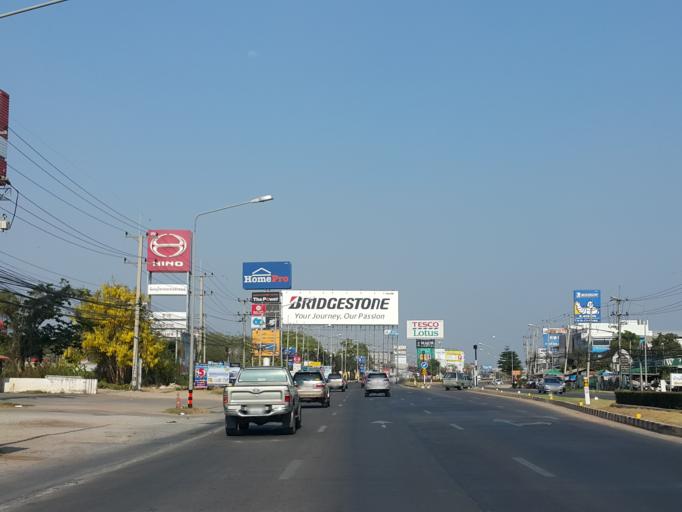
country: TH
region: Phitsanulok
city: Phitsanulok
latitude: 16.8180
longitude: 100.2955
